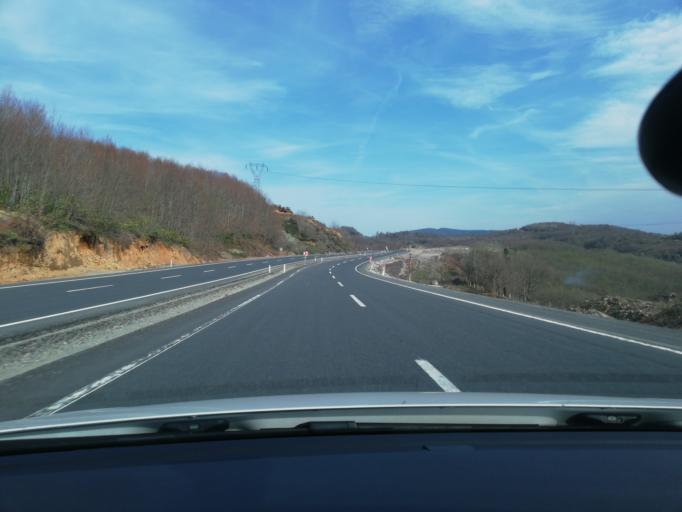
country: TR
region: Zonguldak
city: Eregli
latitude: 41.3311
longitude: 31.5794
